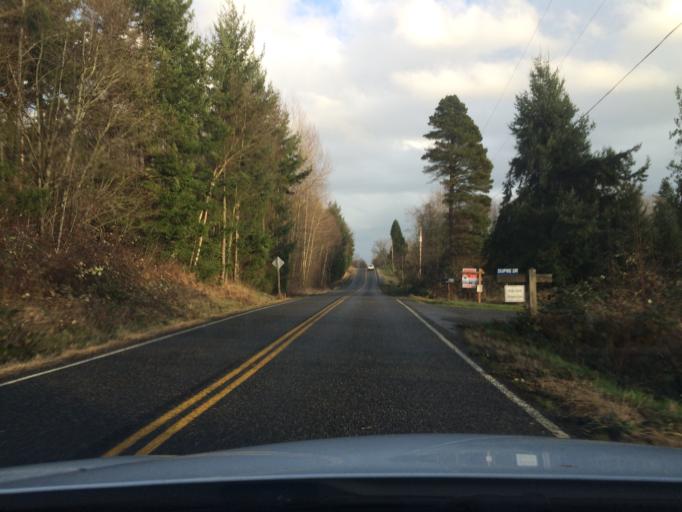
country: CA
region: British Columbia
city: Langley
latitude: 48.9935
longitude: -122.6386
